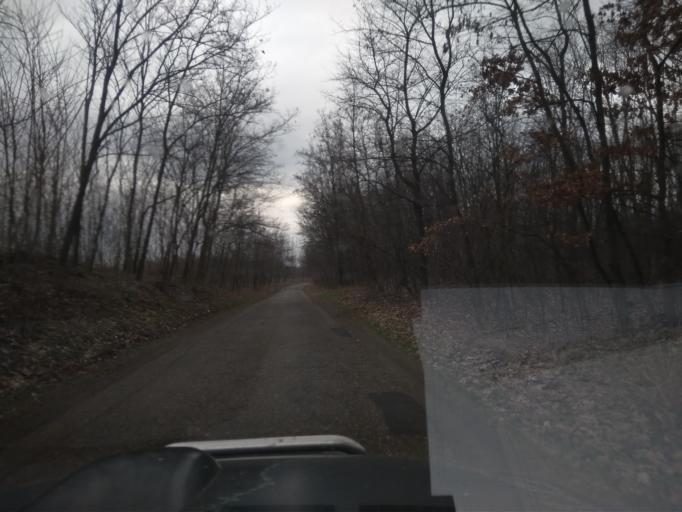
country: HU
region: Szabolcs-Szatmar-Bereg
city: Nyirpazony
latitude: 48.0159
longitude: 21.8095
